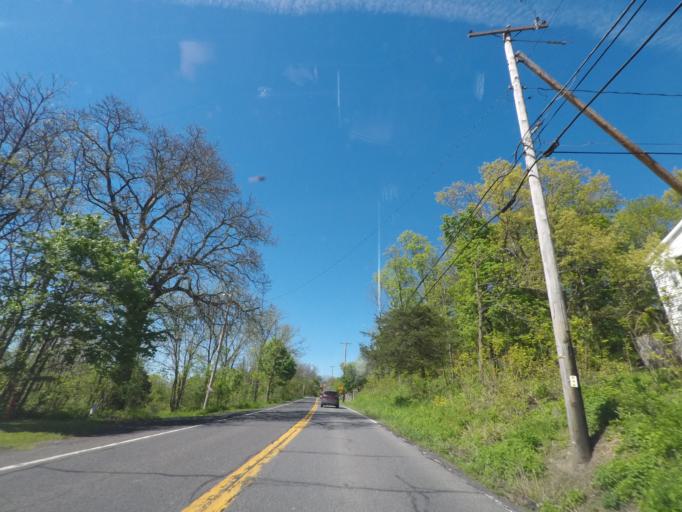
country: US
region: New York
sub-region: Ulster County
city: Saugerties
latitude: 42.1199
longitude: -73.9341
